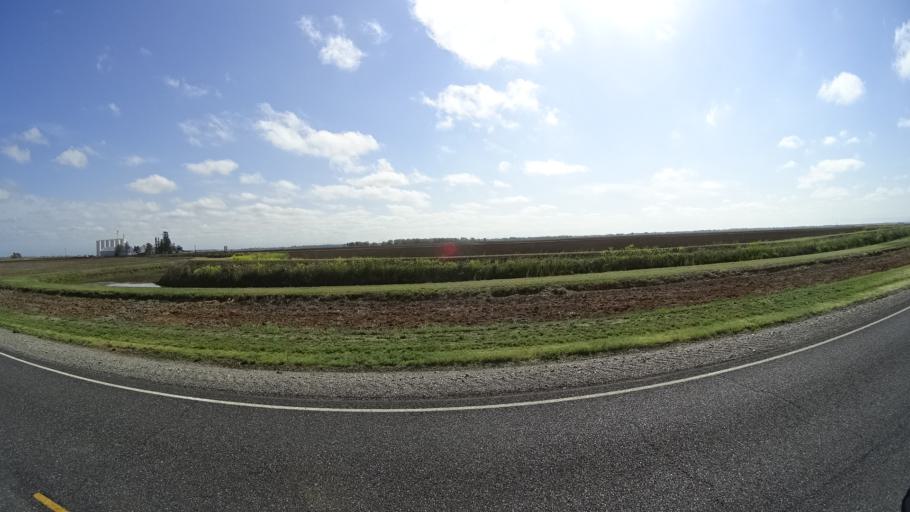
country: US
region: California
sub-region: Butte County
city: Durham
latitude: 39.4900
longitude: -121.9294
